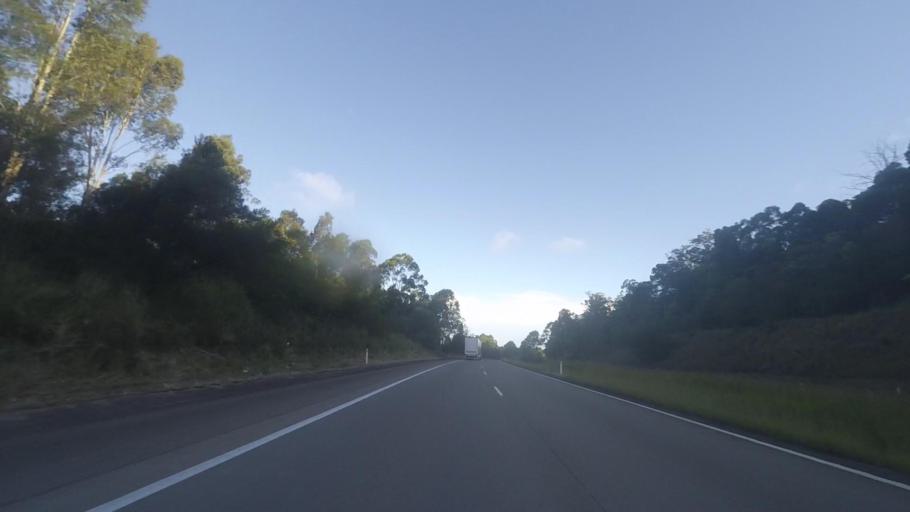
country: AU
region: New South Wales
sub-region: Great Lakes
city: Bulahdelah
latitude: -32.2847
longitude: 152.3390
